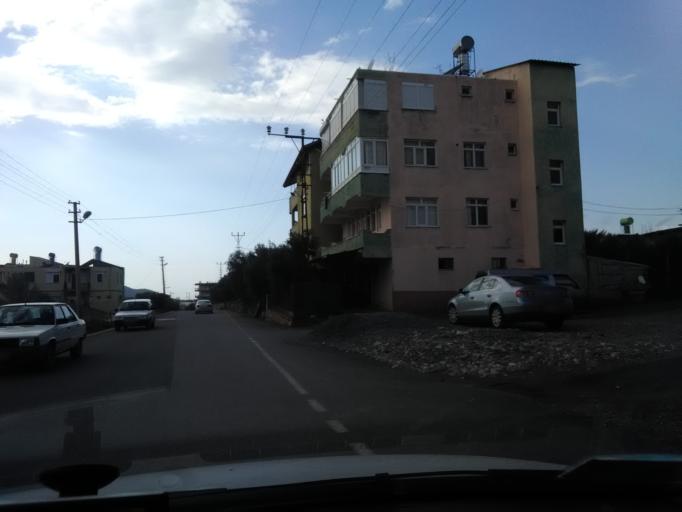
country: TR
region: Antalya
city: Gazipasa
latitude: 36.2742
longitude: 32.3422
